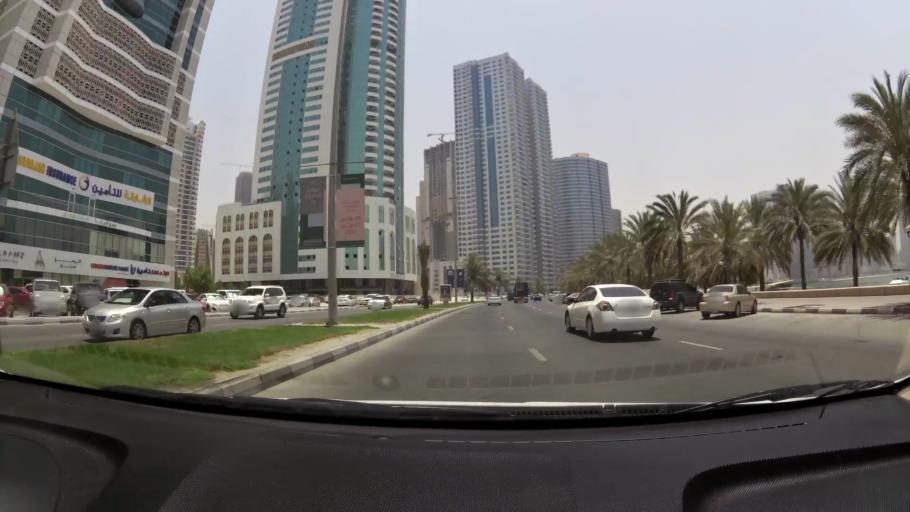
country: AE
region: Ash Shariqah
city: Sharjah
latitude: 25.3265
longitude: 55.3707
